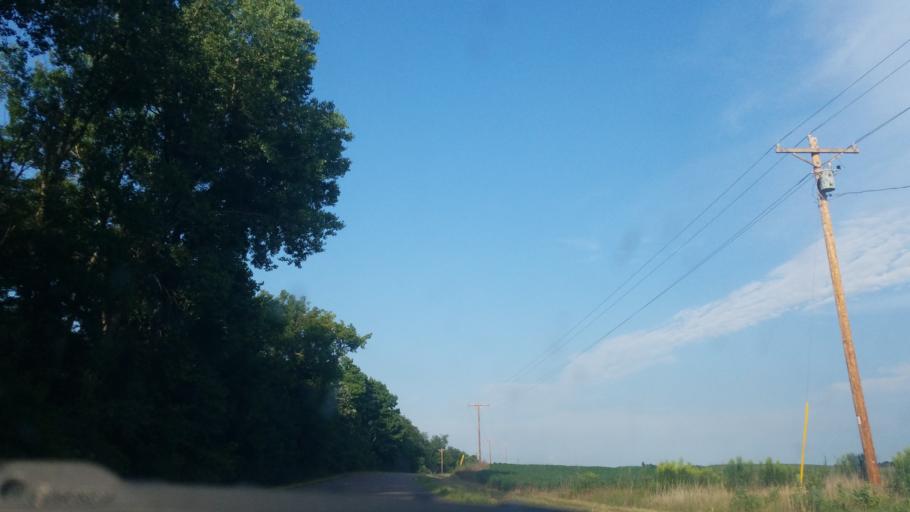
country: US
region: Wisconsin
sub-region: Dunn County
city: Menomonie
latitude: 44.8141
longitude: -91.8927
